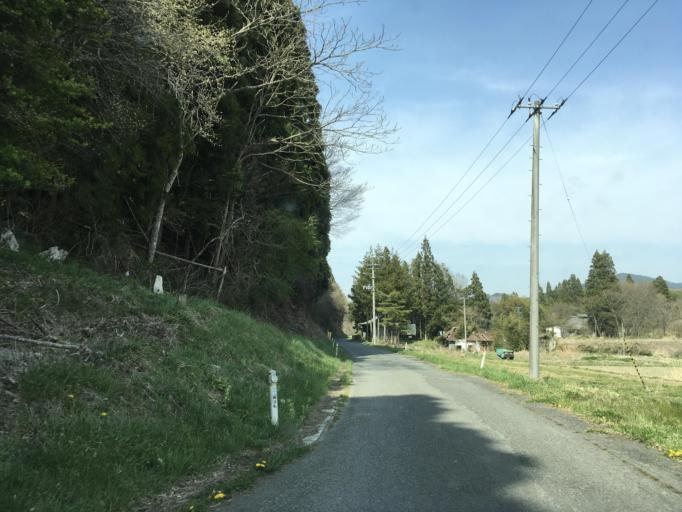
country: JP
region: Iwate
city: Ichinoseki
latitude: 38.8267
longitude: 141.3501
